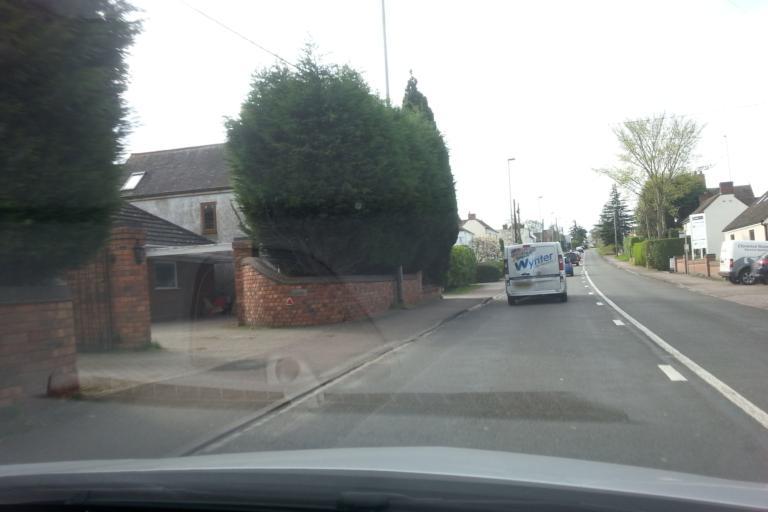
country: GB
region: England
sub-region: Staffordshire
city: Shenstone
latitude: 52.6106
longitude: -1.8376
